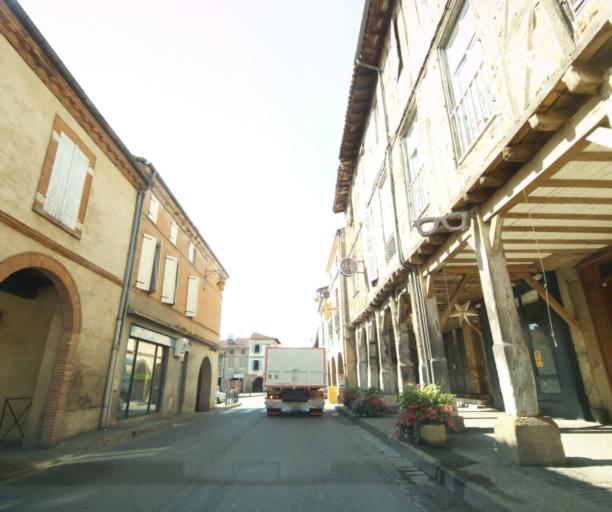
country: FR
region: Midi-Pyrenees
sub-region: Departement de la Haute-Garonne
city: Saint-Sulpice-sur-Leze
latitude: 43.3287
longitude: 1.3222
